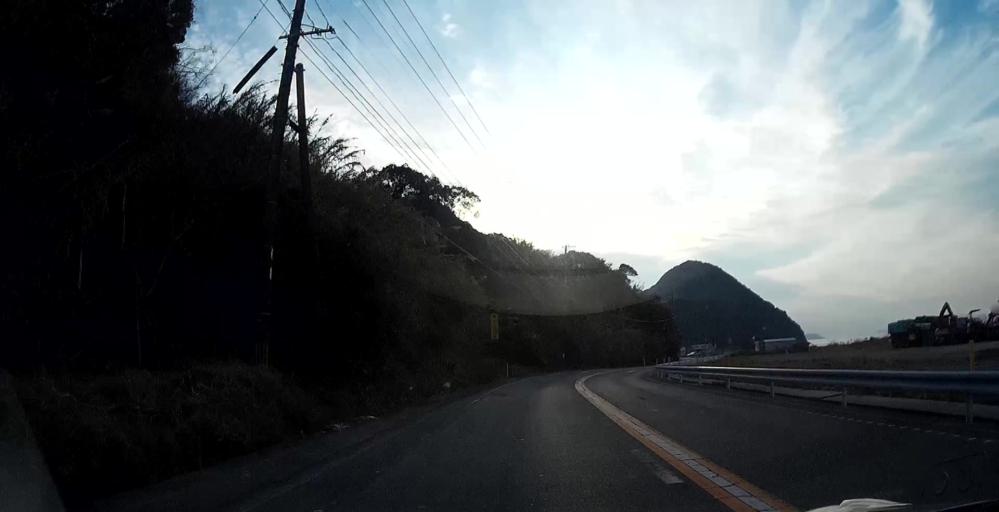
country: JP
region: Nagasaki
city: Shimabara
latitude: 32.6287
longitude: 130.4567
